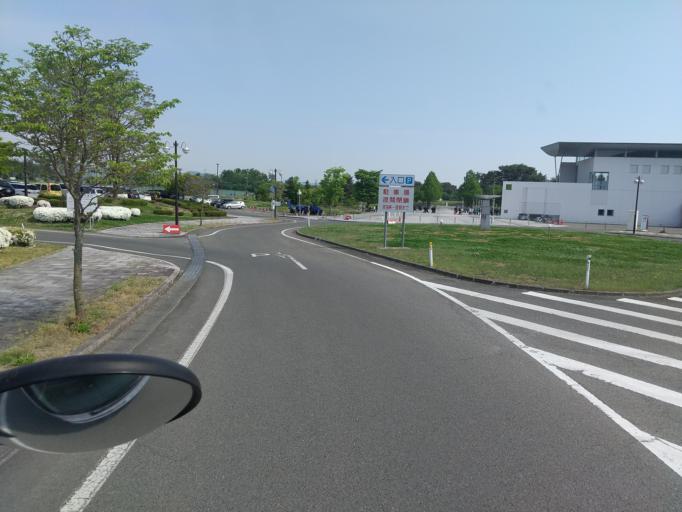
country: JP
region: Iwate
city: Hanamaki
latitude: 39.4056
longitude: 141.0953
